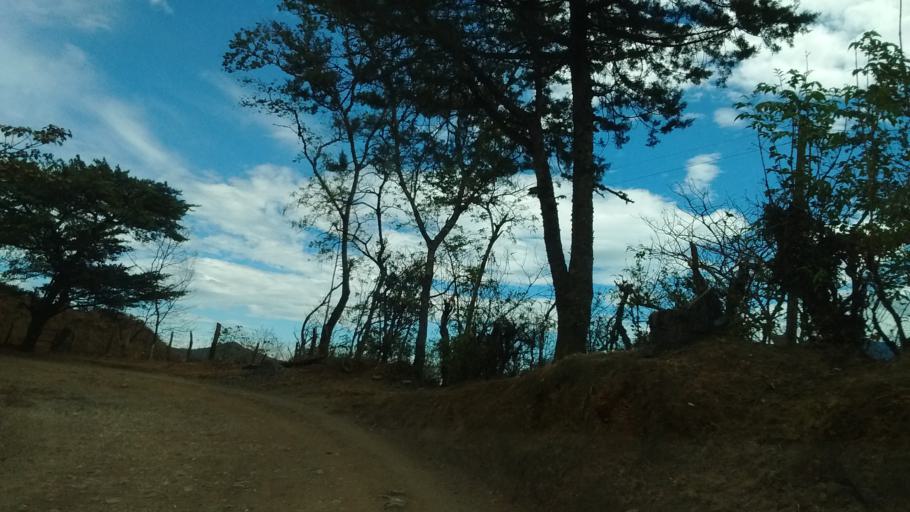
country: CO
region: Cauca
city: Almaguer
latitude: 1.8442
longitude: -76.9114
